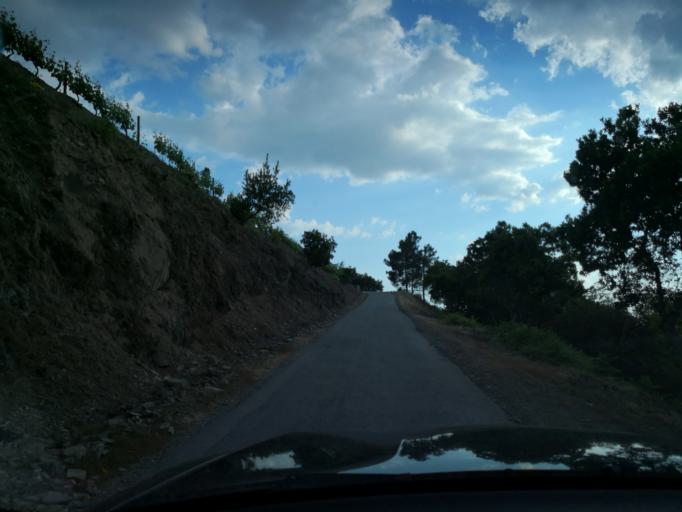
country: PT
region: Vila Real
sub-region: Vila Real
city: Vila Real
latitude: 41.2197
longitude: -7.7068
